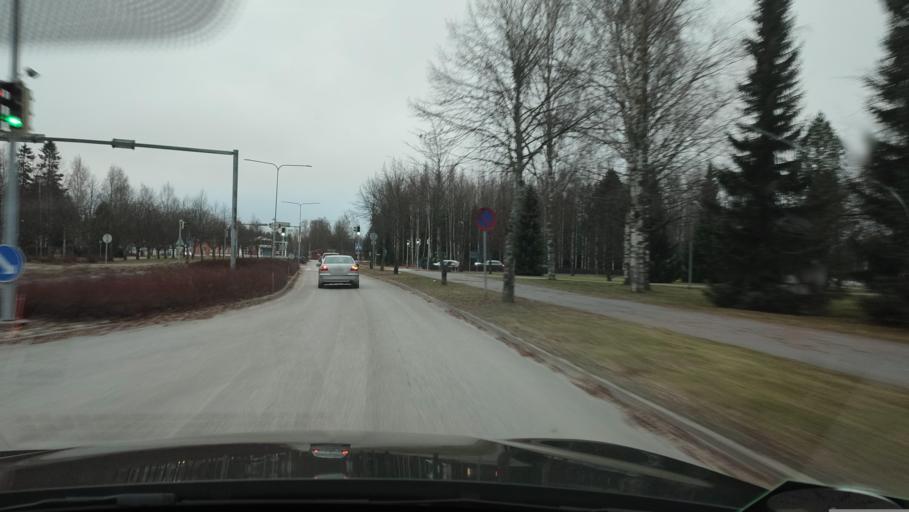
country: FI
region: Southern Ostrobothnia
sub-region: Suupohja
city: Kauhajoki
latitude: 62.4214
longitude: 22.1754
